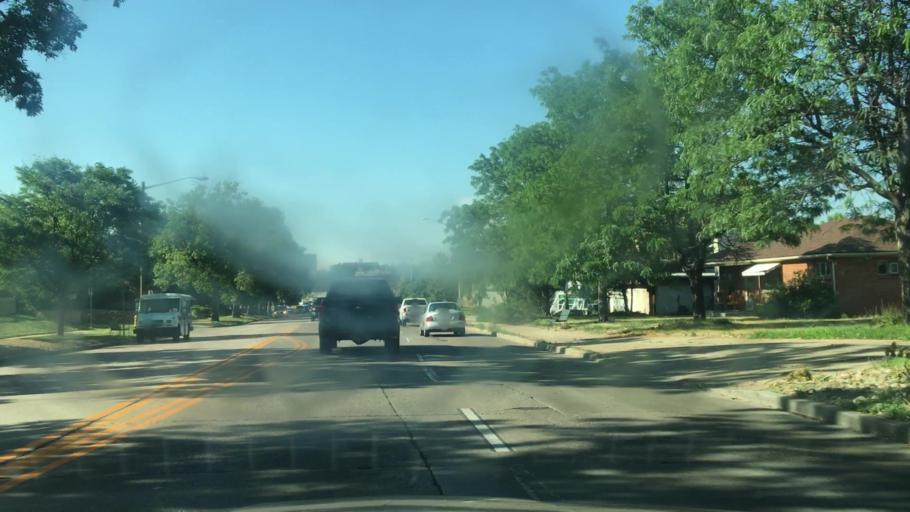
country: US
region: Colorado
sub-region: Arapahoe County
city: Glendale
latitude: 39.6881
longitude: -104.9594
